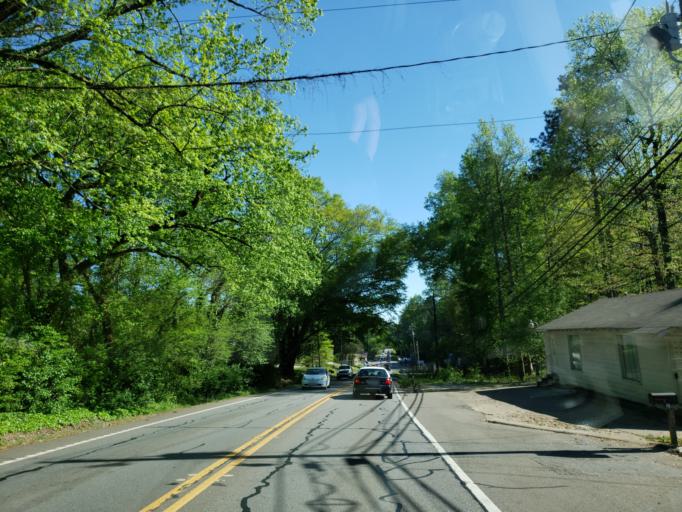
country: US
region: Georgia
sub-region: Cherokee County
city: Canton
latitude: 34.2523
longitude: -84.4939
